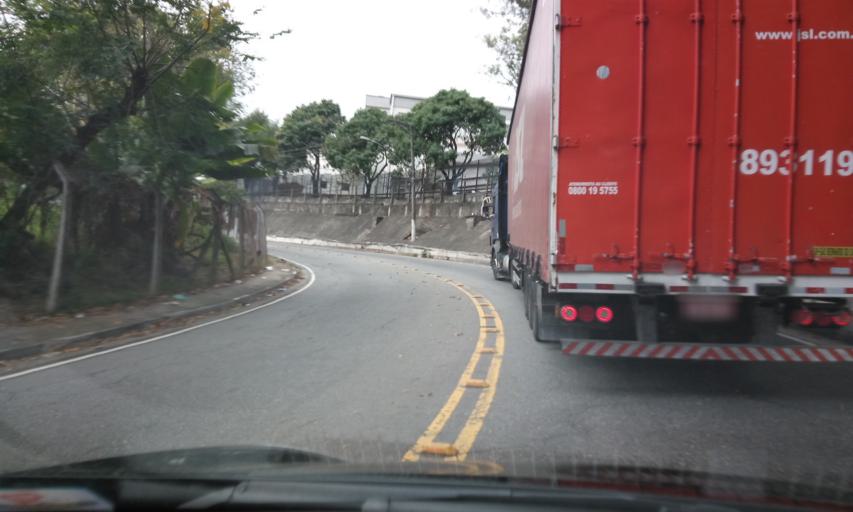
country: BR
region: Sao Paulo
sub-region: Sao Caetano Do Sul
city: Sao Caetano do Sul
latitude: -23.6504
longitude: -46.5838
